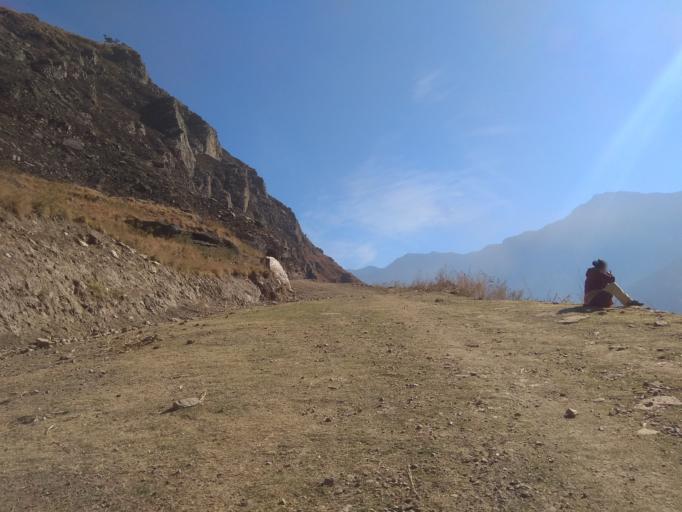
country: NP
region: Mid Western
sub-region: Bheri Zone
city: Dailekh
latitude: 29.2957
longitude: 81.7088
